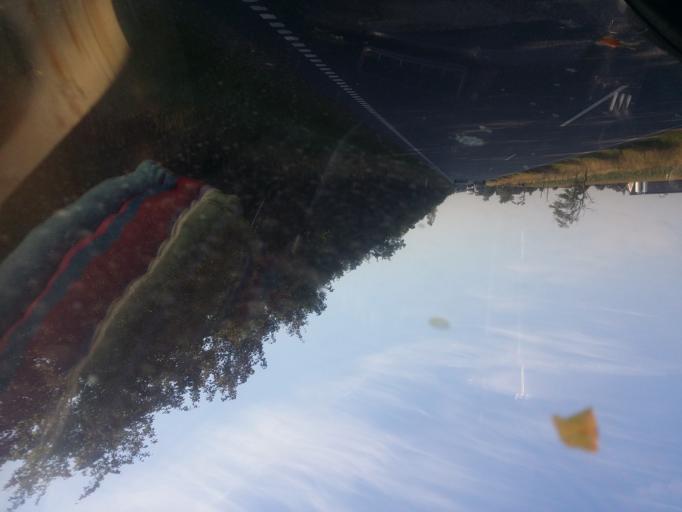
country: DK
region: South Denmark
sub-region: Esbjerg Kommune
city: Ribe
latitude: 55.3072
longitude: 8.7467
